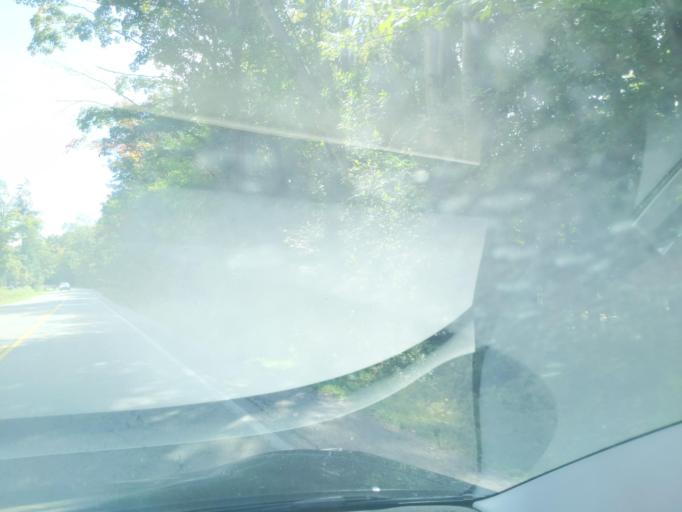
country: US
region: Michigan
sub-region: Antrim County
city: Bellaire
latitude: 45.0775
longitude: -85.3201
